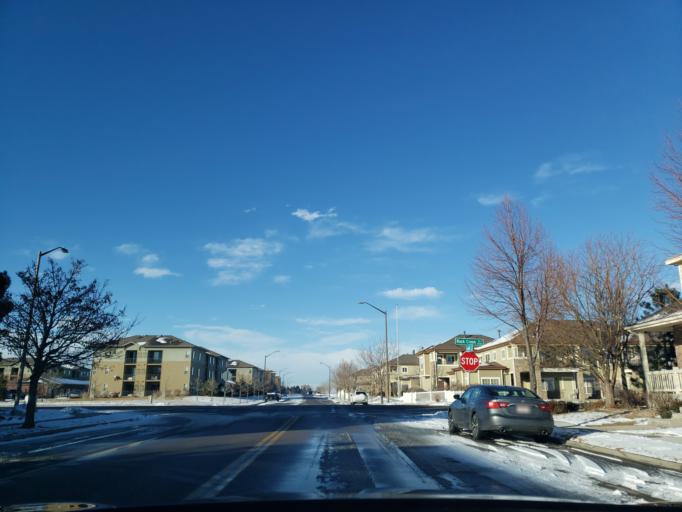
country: US
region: Colorado
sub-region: Larimer County
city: Fort Collins
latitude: 40.5156
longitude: -105.0072
